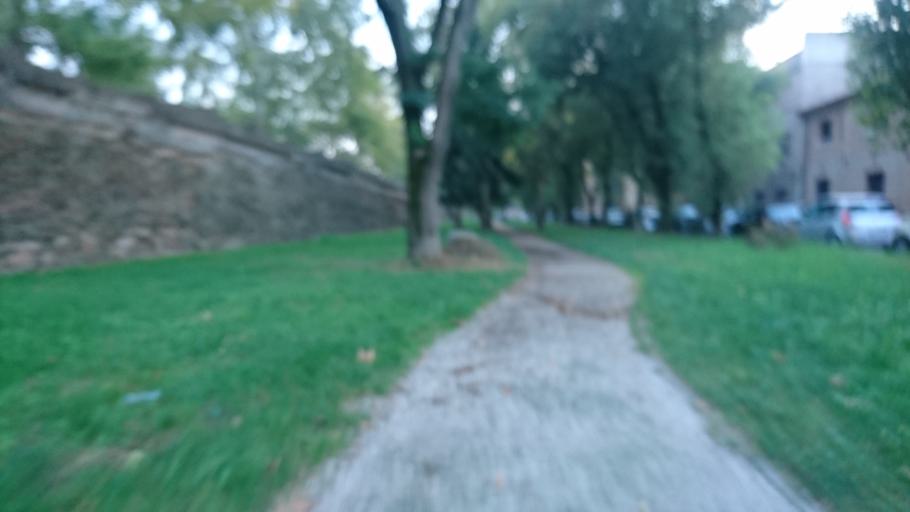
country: IT
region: Emilia-Romagna
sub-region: Provincia di Ferrara
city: Ferrara
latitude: 44.8459
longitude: 11.6111
